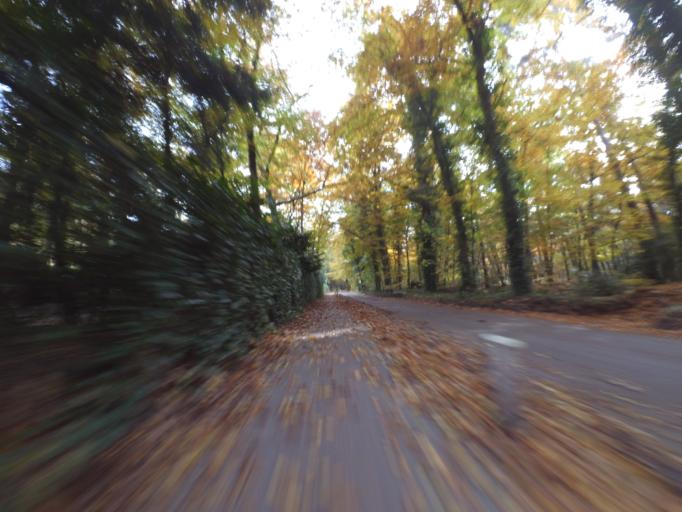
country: NL
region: Gelderland
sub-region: Gemeente Ede
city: Lunteren
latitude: 52.0878
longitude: 5.6336
